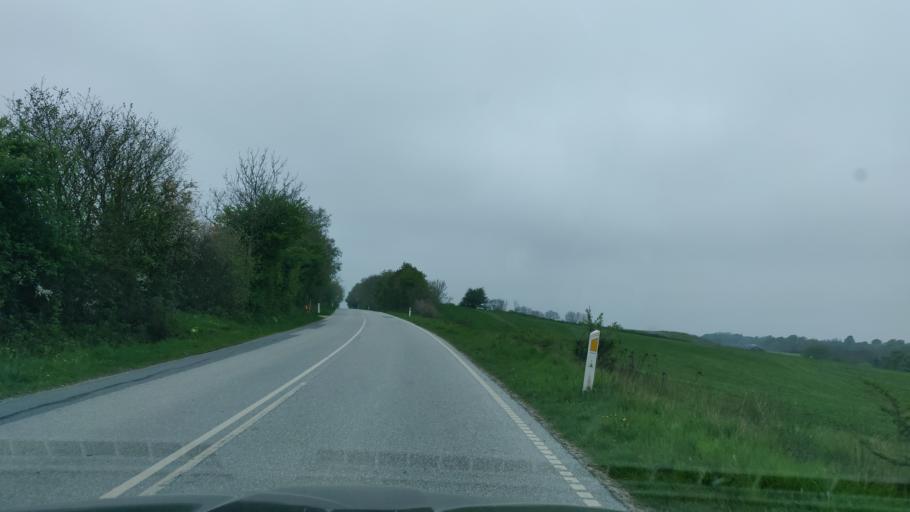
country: DK
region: South Denmark
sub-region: Sonderborg Kommune
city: Guderup
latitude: 55.0003
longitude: 9.9500
